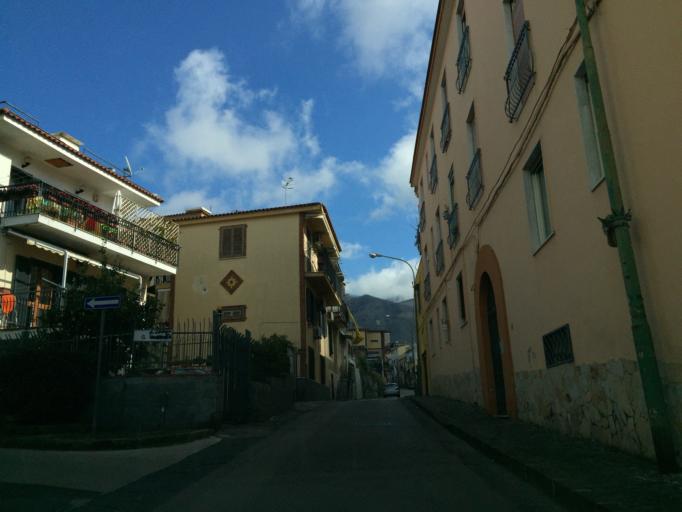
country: IT
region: Campania
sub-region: Provincia di Napoli
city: Massa di Somma
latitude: 40.8419
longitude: 14.3730
